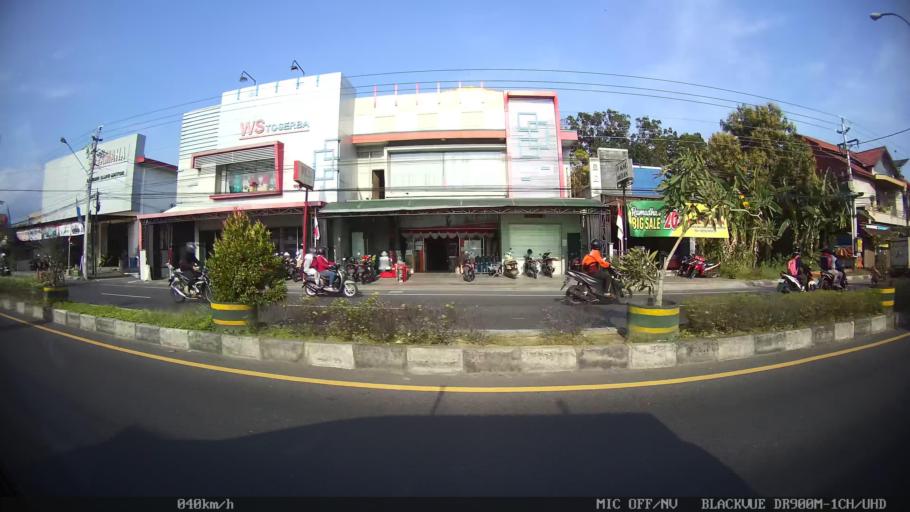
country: ID
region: Daerah Istimewa Yogyakarta
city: Bantul
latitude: -7.8768
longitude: 110.3351
